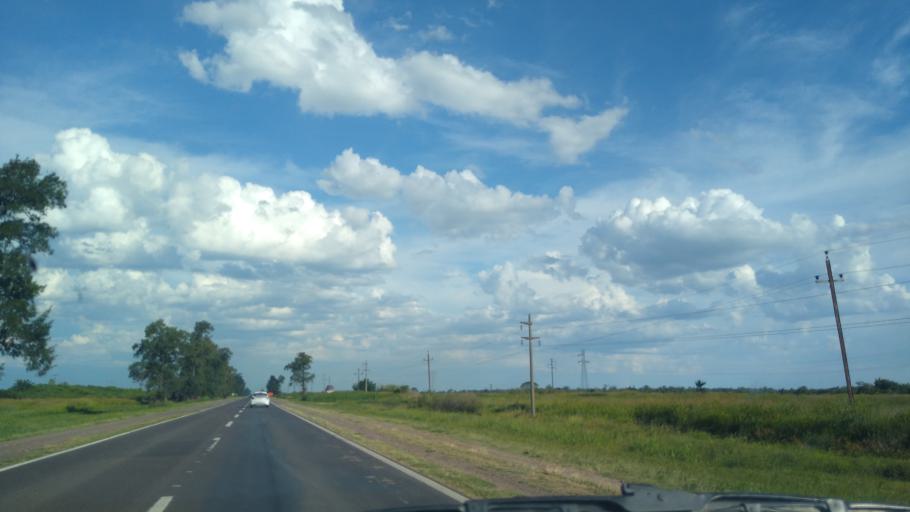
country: AR
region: Chaco
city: Presidencia Roque Saenz Pena
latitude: -26.8184
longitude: -60.4017
